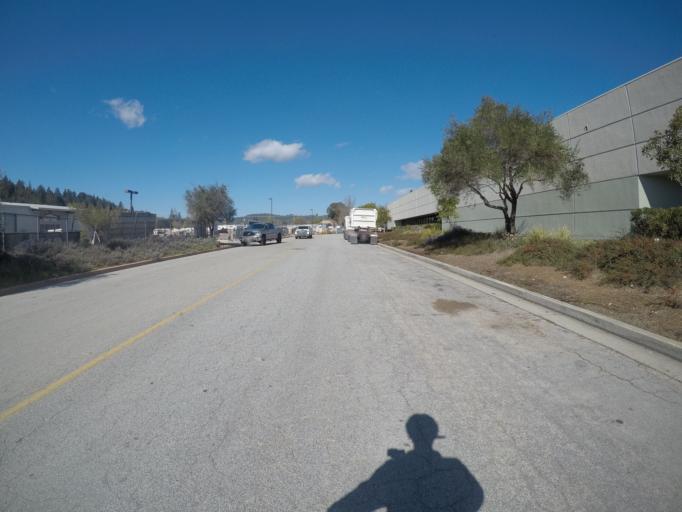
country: US
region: California
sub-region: Santa Cruz County
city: Scotts Valley
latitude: 37.0517
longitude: -122.0111
